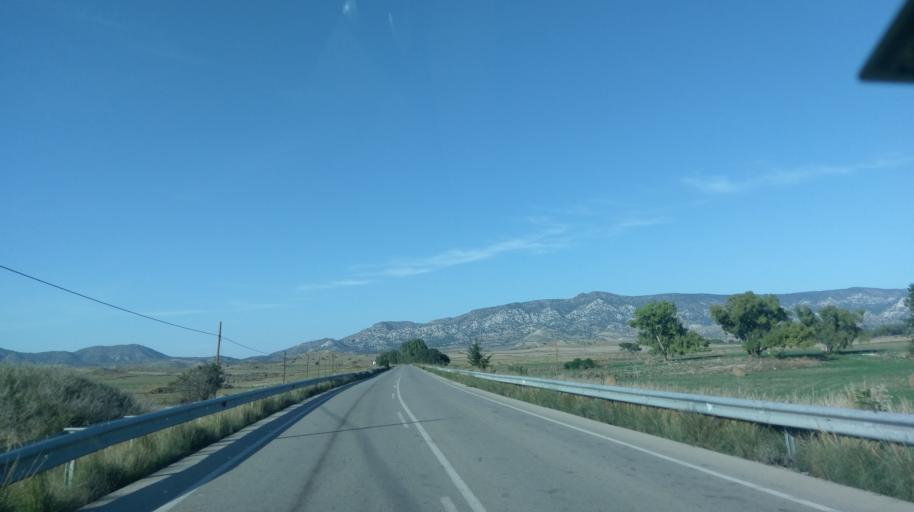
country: CY
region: Ammochostos
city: Lefkonoiko
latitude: 35.2974
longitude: 33.7352
